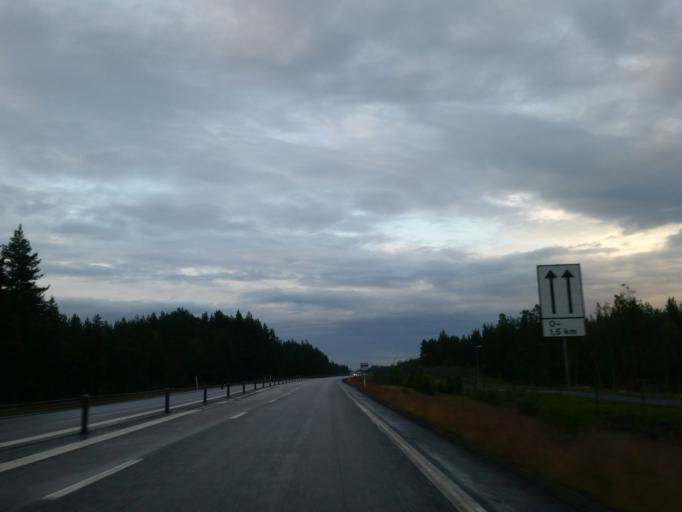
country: SE
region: Vaesterbotten
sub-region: Umea Kommun
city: Taftea
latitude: 63.8820
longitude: 20.4896
